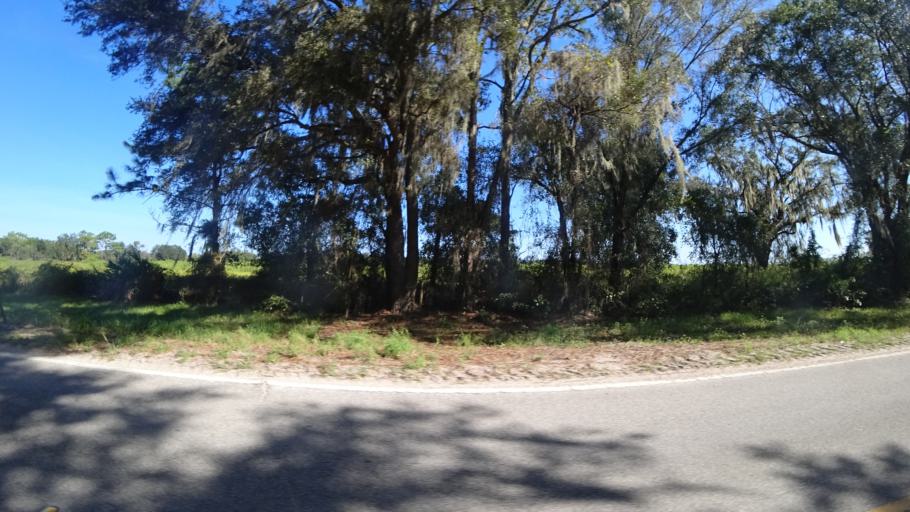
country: US
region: Florida
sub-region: Hillsborough County
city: Wimauma
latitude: 27.6614
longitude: -82.2956
